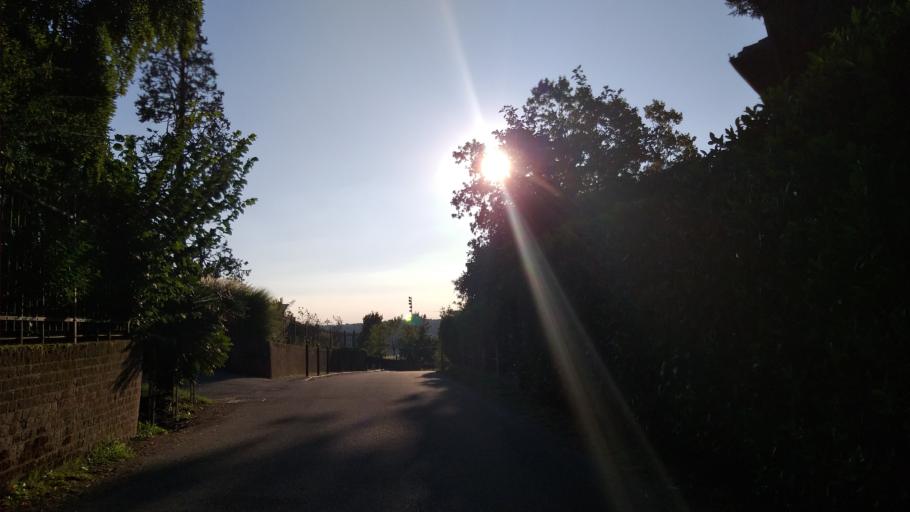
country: IT
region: Piedmont
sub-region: Provincia di Asti
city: Asti
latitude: 44.9243
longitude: 8.1876
